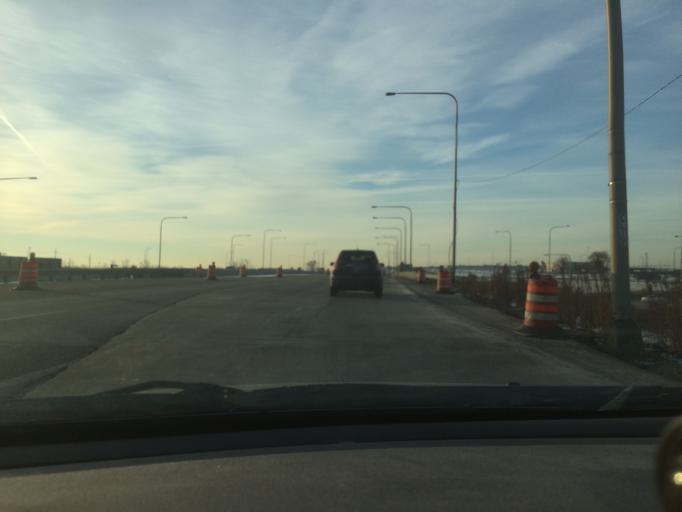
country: US
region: Illinois
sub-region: Cook County
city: Rosemont
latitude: 41.9819
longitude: -87.8792
